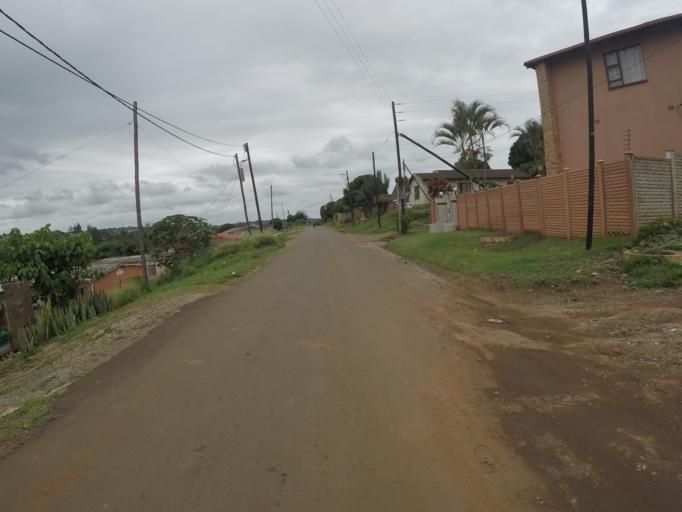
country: ZA
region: KwaZulu-Natal
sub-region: uThungulu District Municipality
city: Empangeni
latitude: -28.7664
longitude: 31.8600
